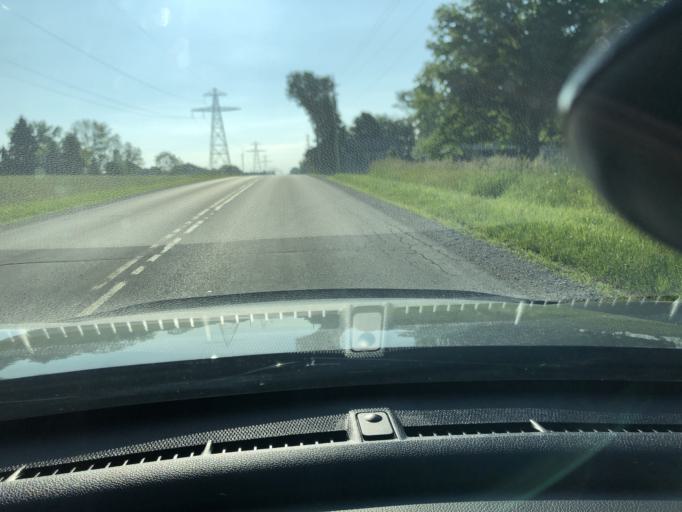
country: CA
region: Ontario
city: Stratford
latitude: 43.3883
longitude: -80.9043
